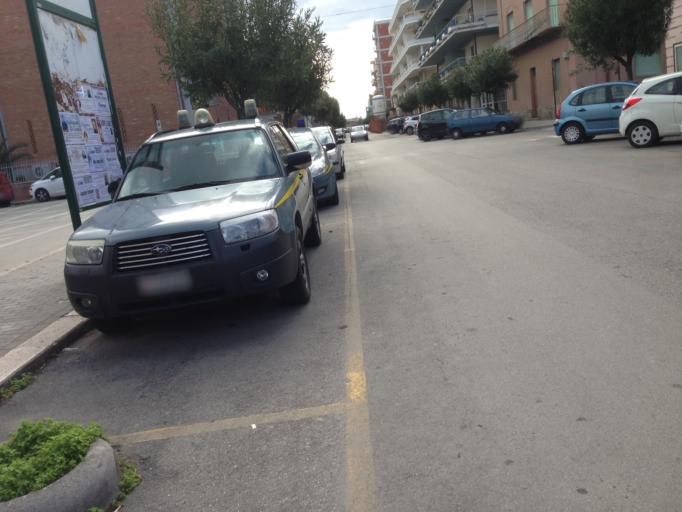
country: IT
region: Molise
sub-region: Provincia di Campobasso
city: Termoli
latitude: 42.0003
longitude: 14.9967
